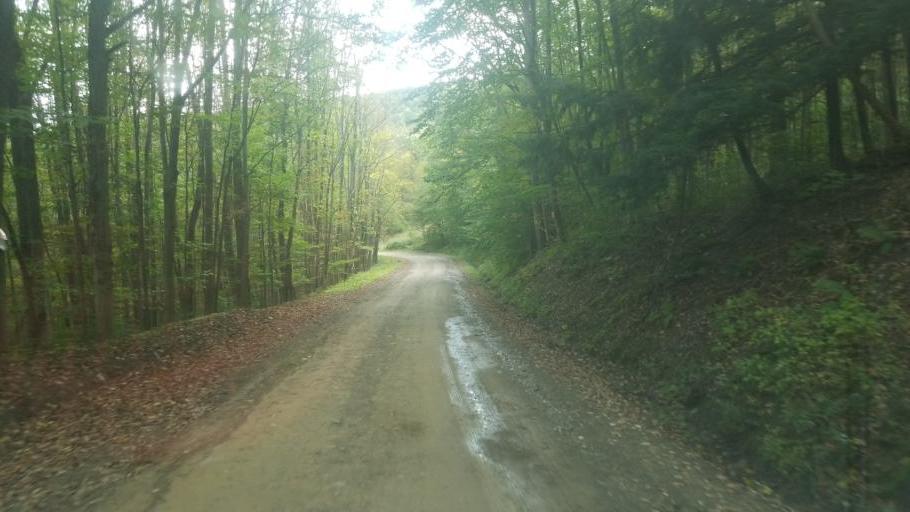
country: US
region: New York
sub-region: Allegany County
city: Cuba
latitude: 42.1439
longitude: -78.3012
